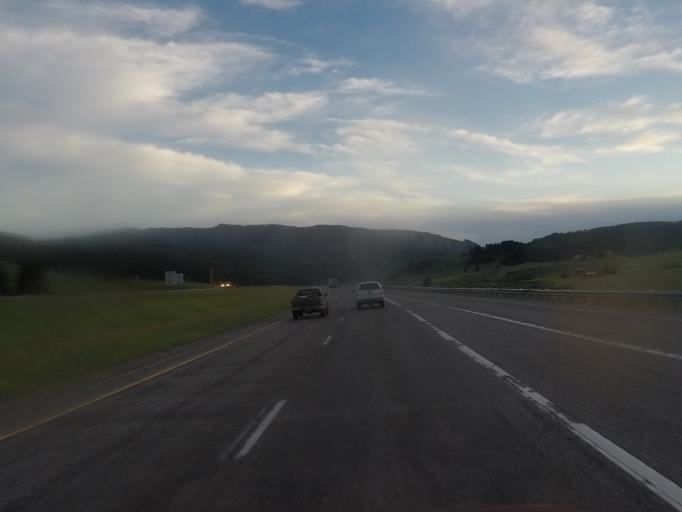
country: US
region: Montana
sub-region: Gallatin County
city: Bozeman
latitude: 45.6637
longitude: -110.8395
